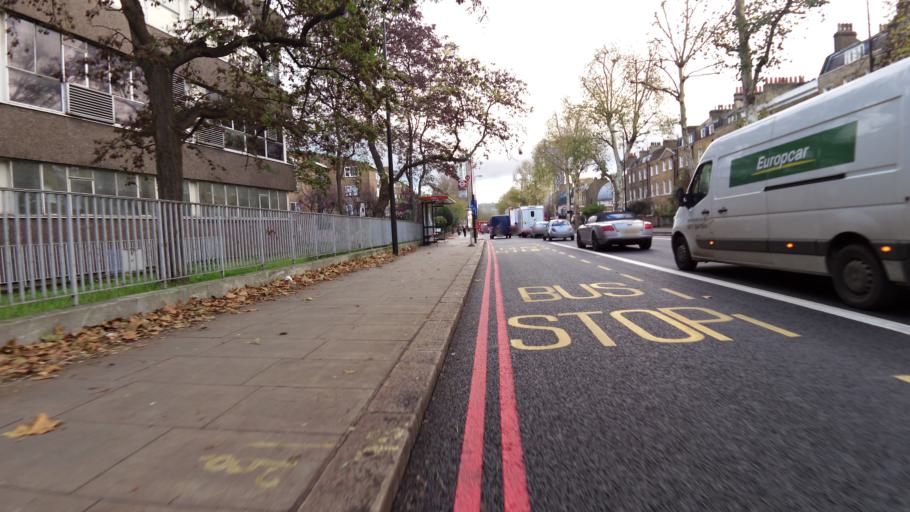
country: GB
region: England
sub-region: Greater London
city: Kennington
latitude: 51.4875
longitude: -0.1068
